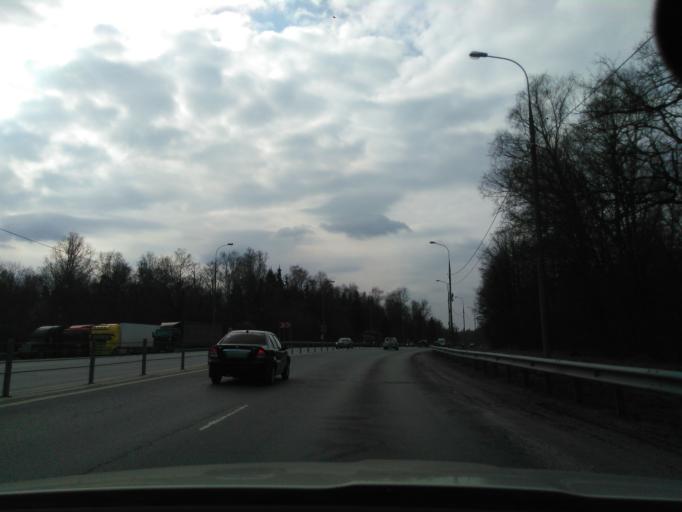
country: RU
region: Moskovskaya
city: Marfino
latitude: 56.0362
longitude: 37.5427
